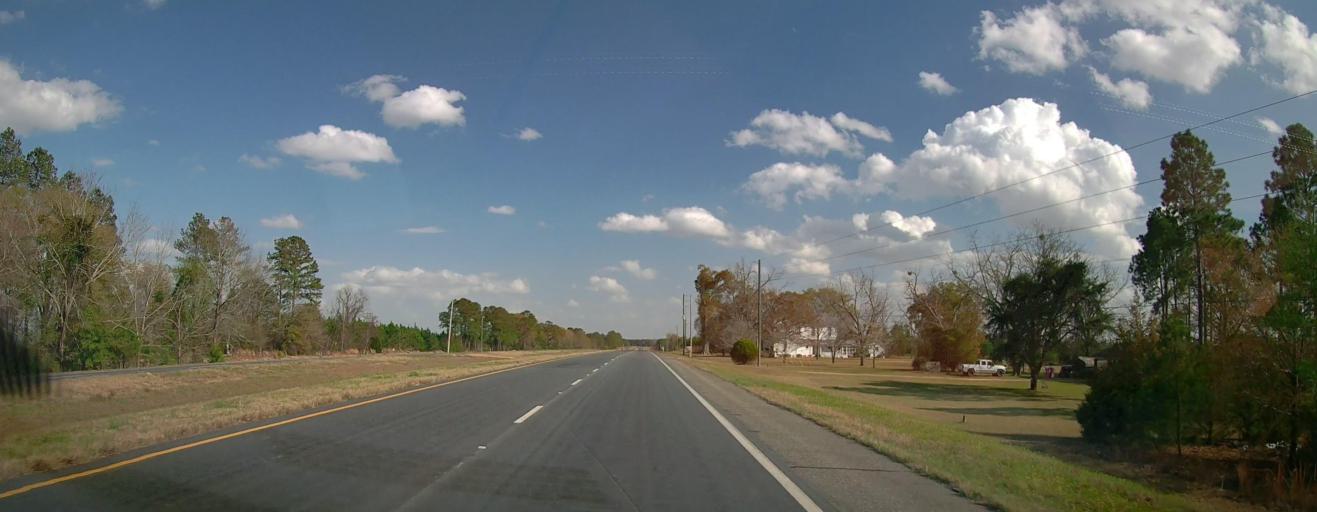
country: US
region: Georgia
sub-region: Dodge County
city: Eastman
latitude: 32.1187
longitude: -83.1099
